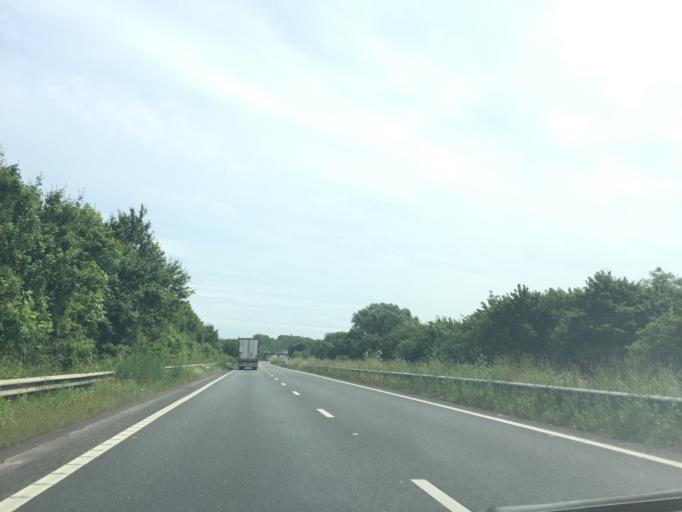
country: GB
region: England
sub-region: Kent
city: Canterbury
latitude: 51.2731
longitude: 1.0555
